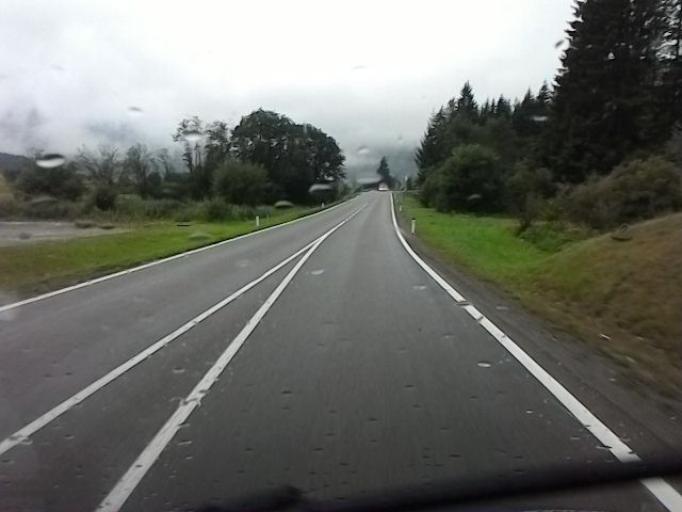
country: AT
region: Tyrol
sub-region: Politischer Bezirk Reutte
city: Ehrwald
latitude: 47.4066
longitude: 10.9032
